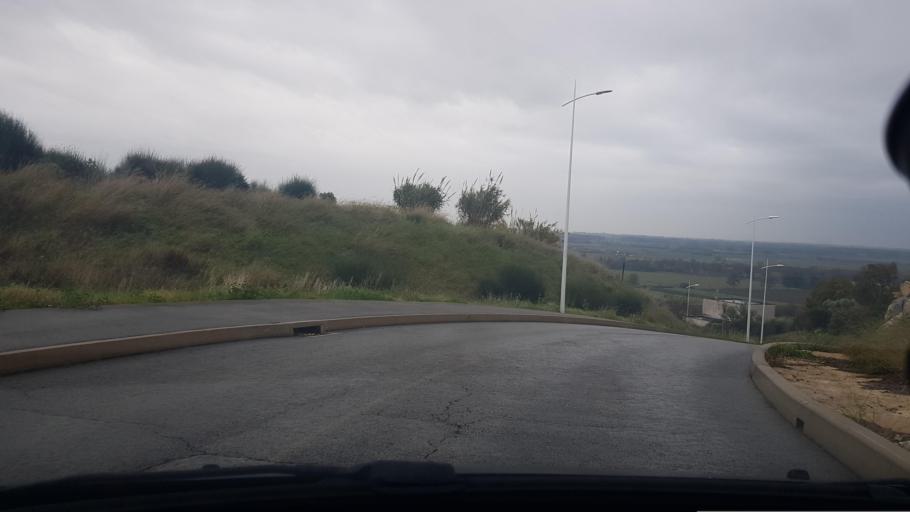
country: FR
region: Languedoc-Roussillon
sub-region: Departement du Gard
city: Bellegarde
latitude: 43.7504
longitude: 4.4996
